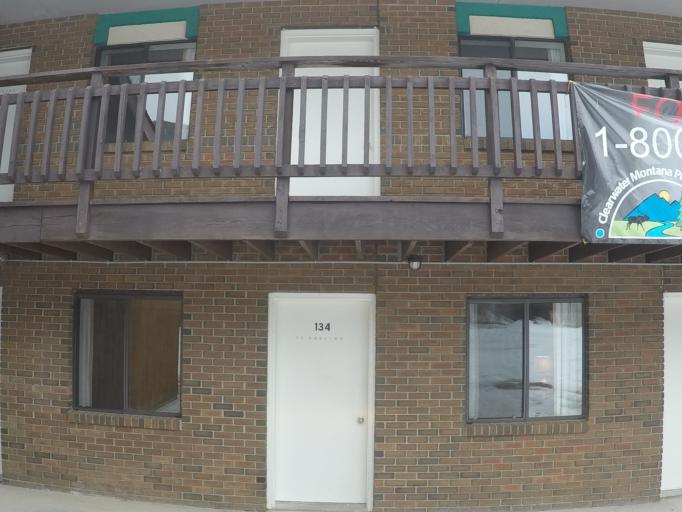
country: US
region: Montana
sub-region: Meagher County
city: White Sulphur Springs
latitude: 46.9335
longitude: -110.7363
